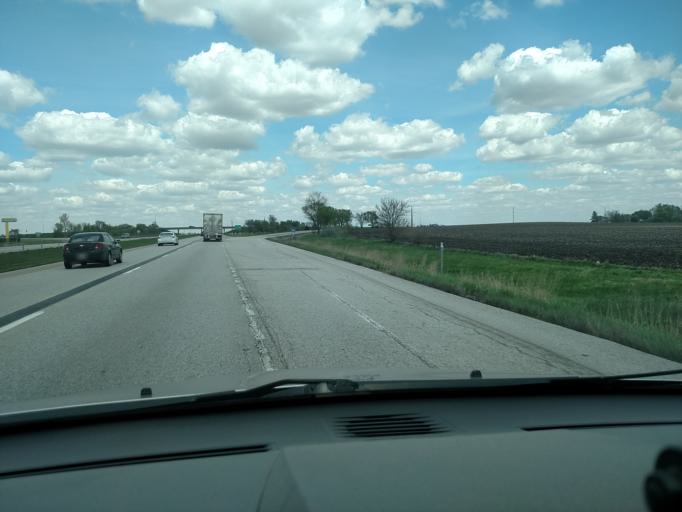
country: US
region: Iowa
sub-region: Polk County
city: Ankeny
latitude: 41.7864
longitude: -93.5704
